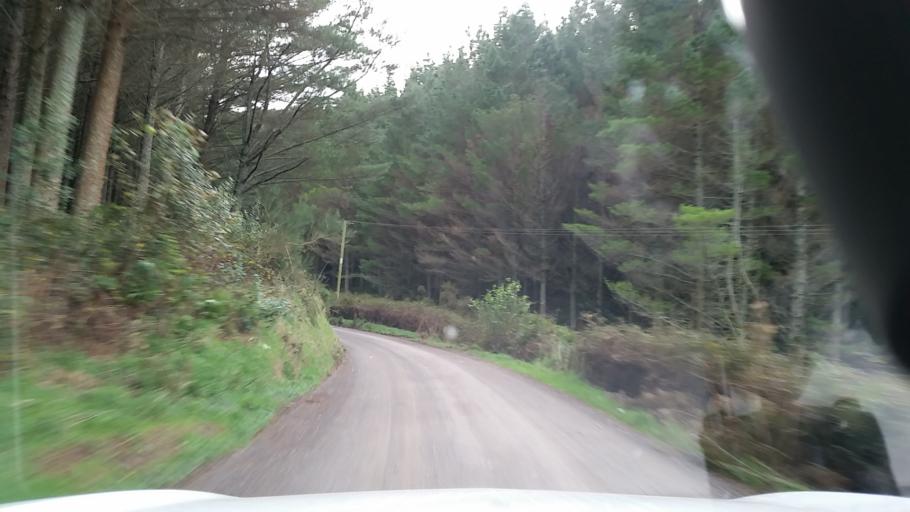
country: NZ
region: Bay of Plenty
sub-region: Rotorua District
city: Rotorua
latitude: -38.2234
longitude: 176.1611
